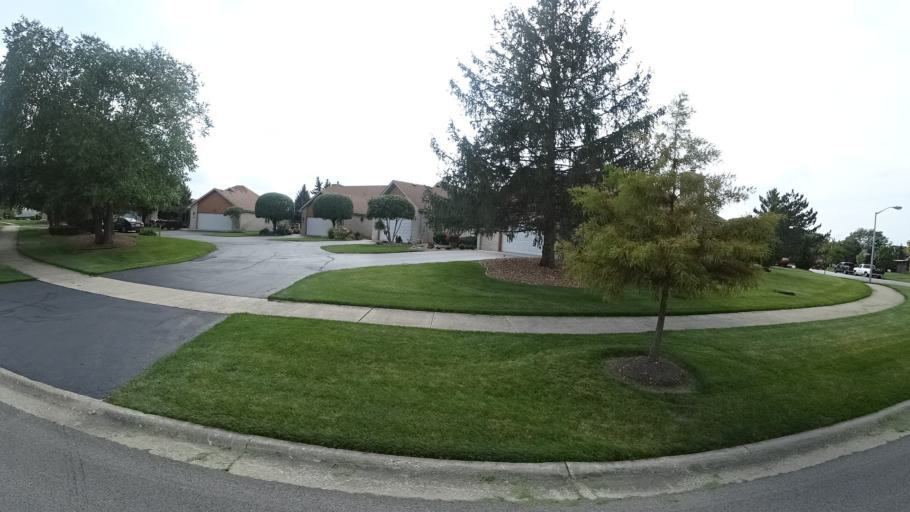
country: US
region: Illinois
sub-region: Cook County
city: Tinley Park
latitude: 41.5576
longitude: -87.7754
